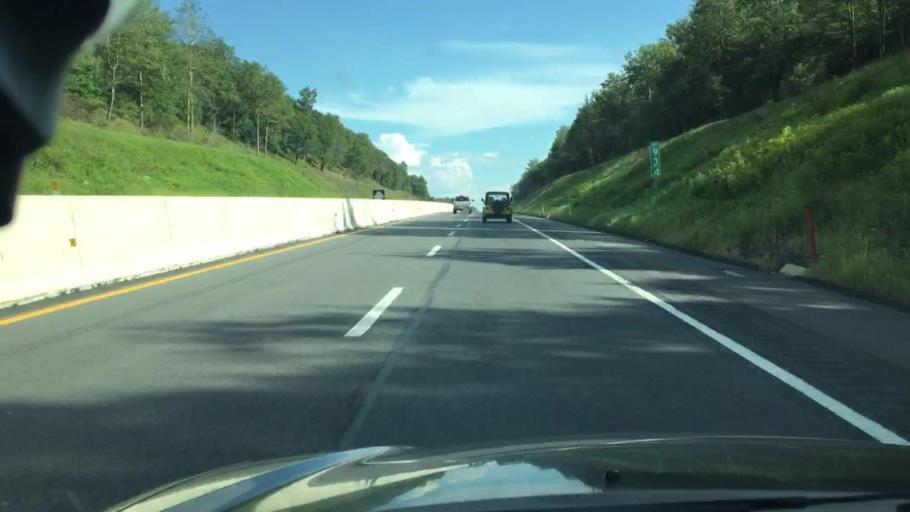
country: US
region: Pennsylvania
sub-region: Luzerne County
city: White Haven
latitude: 41.0621
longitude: -75.6873
